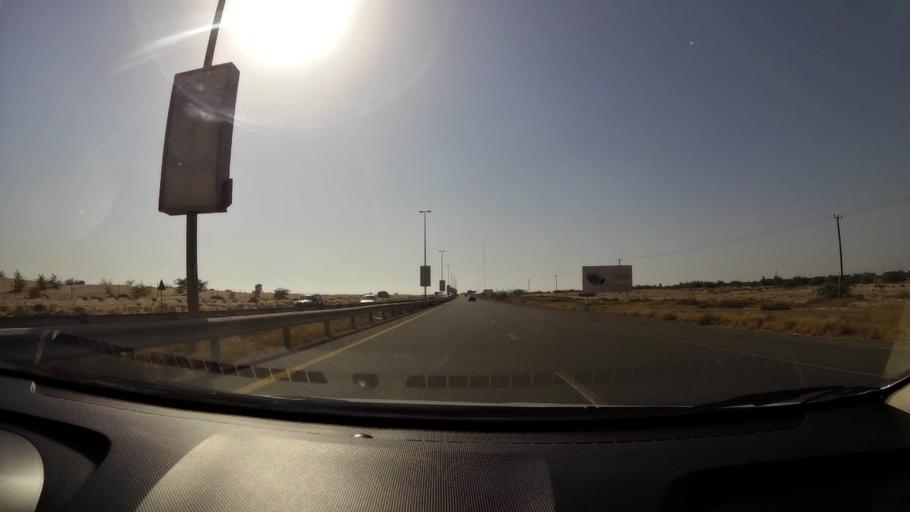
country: AE
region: Umm al Qaywayn
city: Umm al Qaywayn
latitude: 25.4730
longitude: 55.5766
